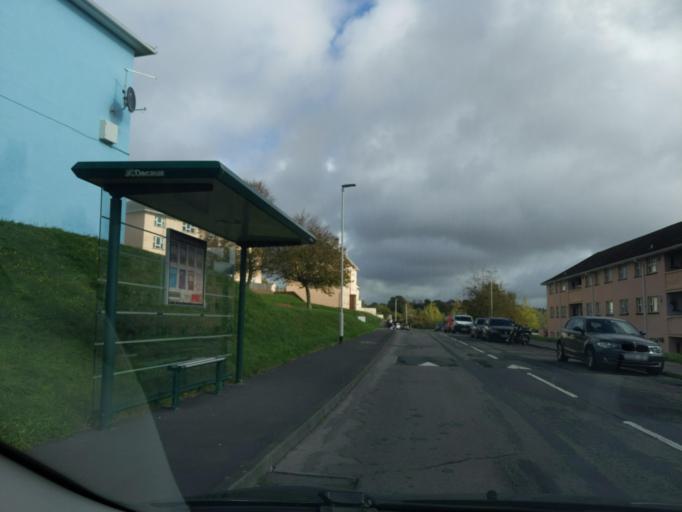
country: GB
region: England
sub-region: Cornwall
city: Torpoint
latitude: 50.3981
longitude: -4.1873
